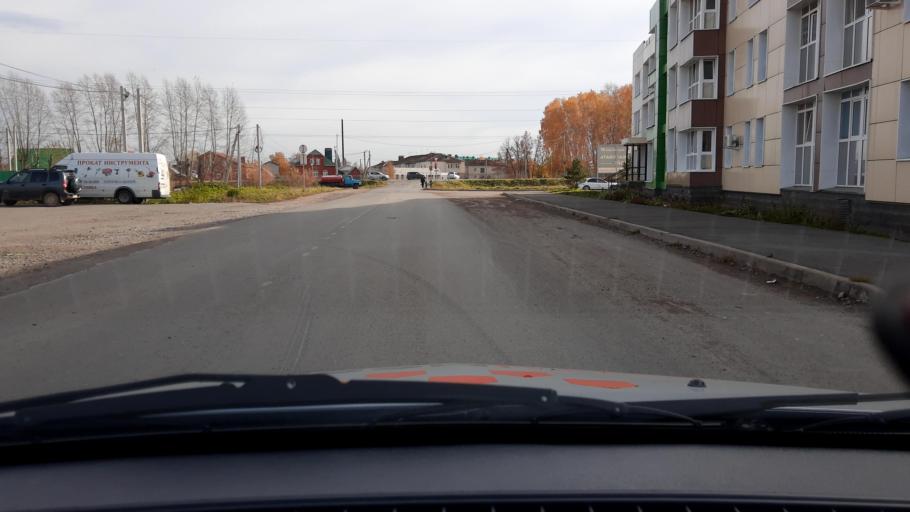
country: RU
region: Bashkortostan
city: Mikhaylovka
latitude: 54.7847
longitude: 55.8345
